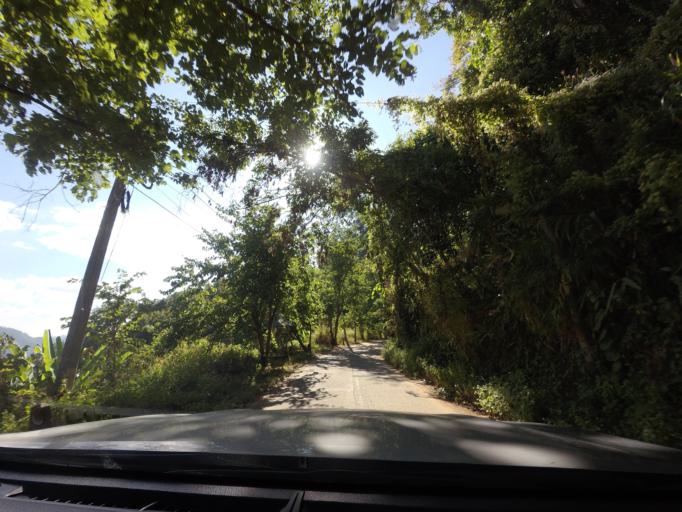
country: TH
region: Lampang
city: Mueang Pan
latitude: 18.8306
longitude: 99.3939
